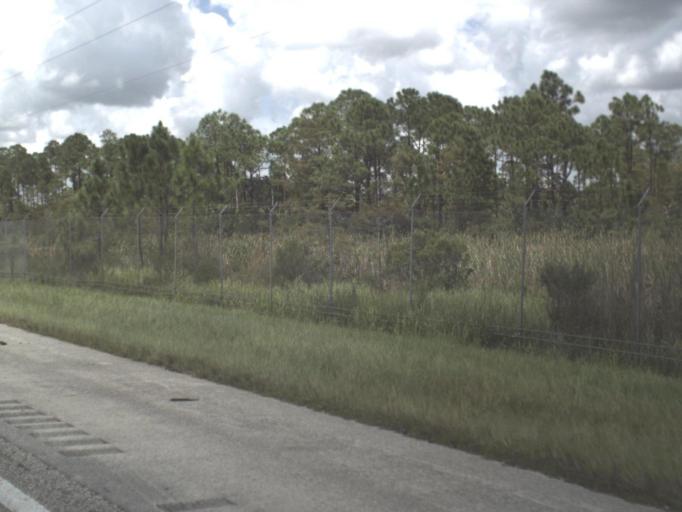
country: US
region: Florida
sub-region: Collier County
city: Immokalee
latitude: 26.1710
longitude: -80.9654
